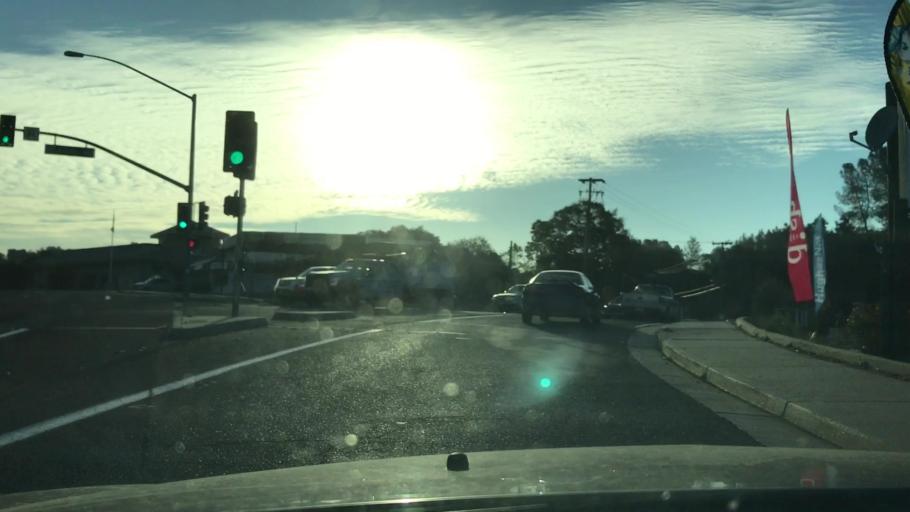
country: US
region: California
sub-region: Tuolumne County
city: East Sonora
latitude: 37.9746
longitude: -120.3465
